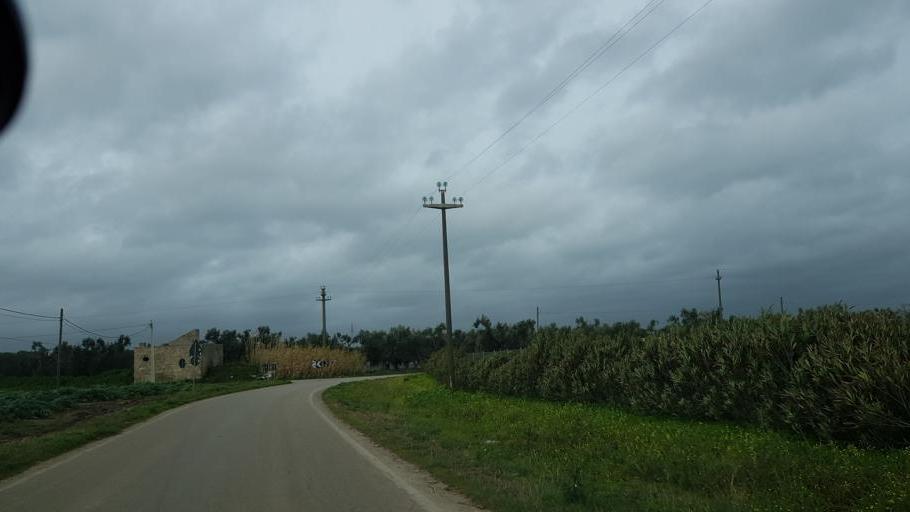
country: IT
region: Apulia
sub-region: Provincia di Brindisi
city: Brindisi
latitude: 40.5951
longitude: 17.9016
